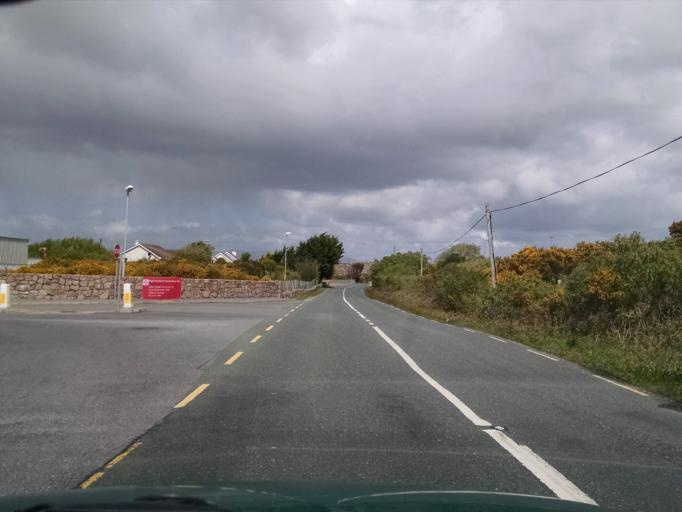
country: IE
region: Connaught
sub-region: County Galway
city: Oughterard
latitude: 53.2924
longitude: -9.5496
